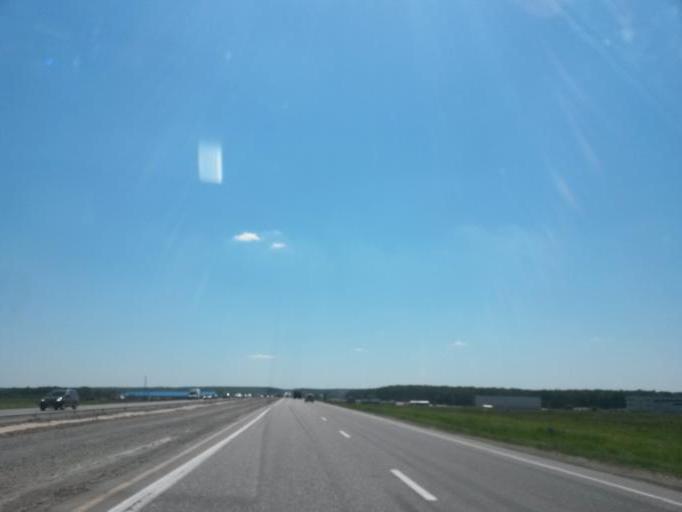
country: RU
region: Moskovskaya
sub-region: Chekhovskiy Rayon
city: Chekhov
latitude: 55.1481
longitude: 37.5528
